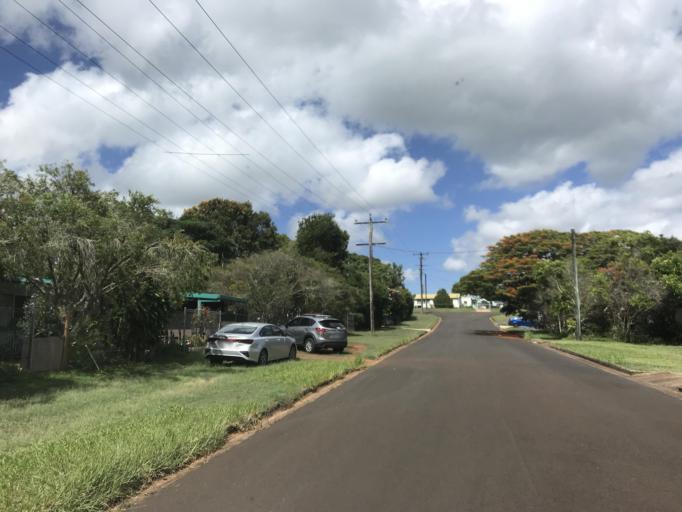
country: AU
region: Queensland
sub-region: Tablelands
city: Tolga
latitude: -17.2241
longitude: 145.4762
